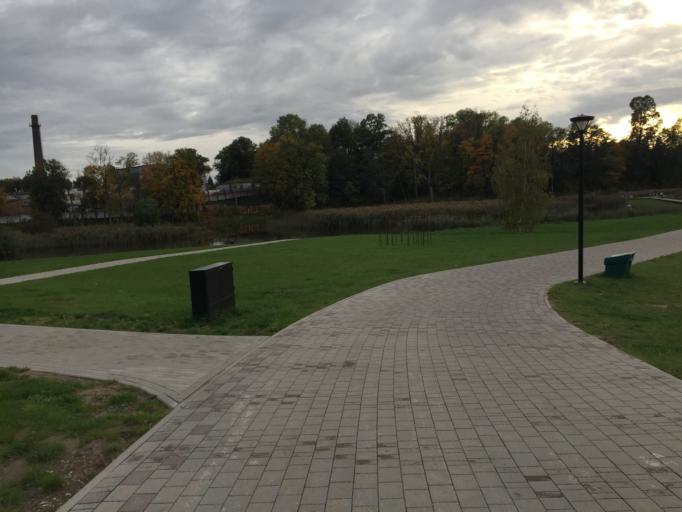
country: LV
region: Dobeles Rajons
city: Dobele
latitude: 56.6226
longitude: 23.2780
